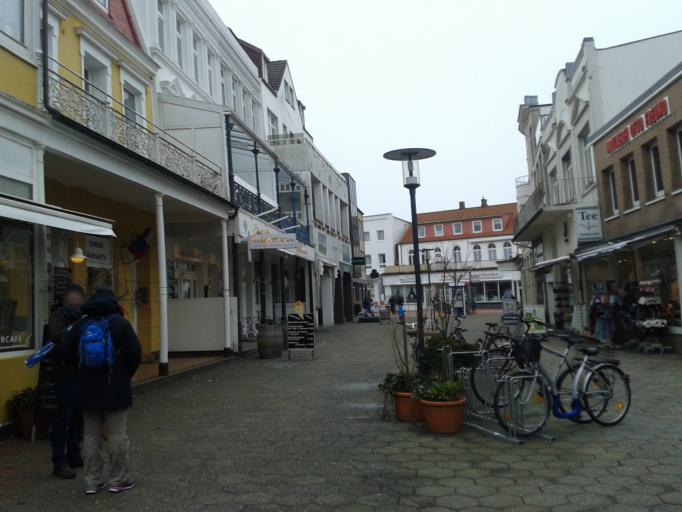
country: DE
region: Lower Saxony
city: Norderney
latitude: 53.7071
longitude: 7.1433
